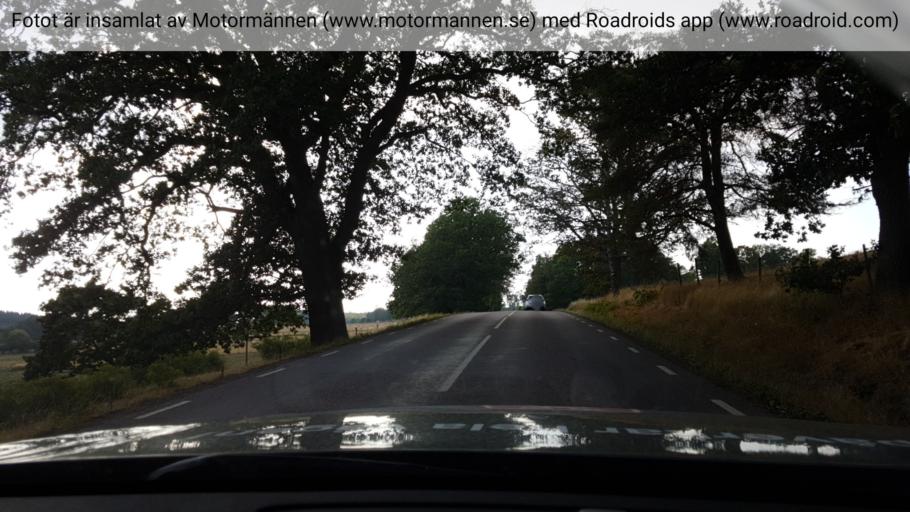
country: SE
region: Soedermanland
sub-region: Gnesta Kommun
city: Gnesta
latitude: 59.0787
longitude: 17.2784
